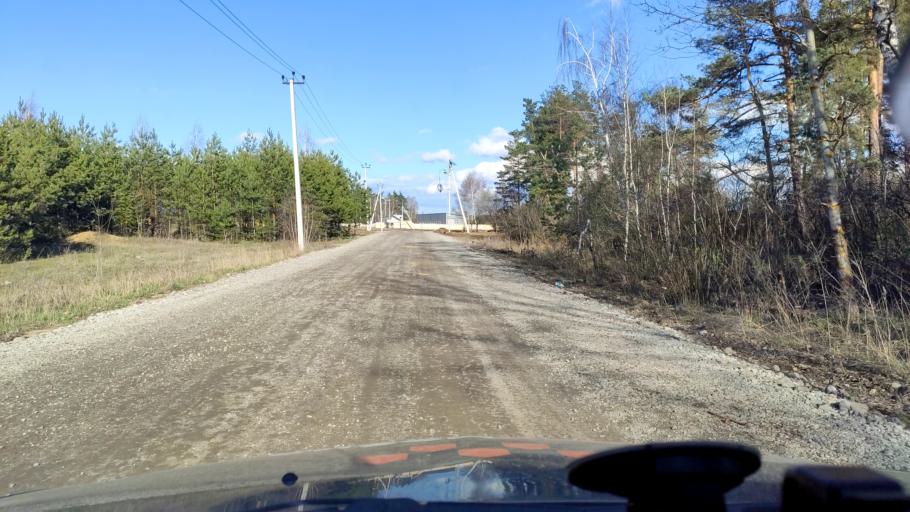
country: RU
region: Voronezj
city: Podgornoye
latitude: 51.8297
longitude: 39.1972
